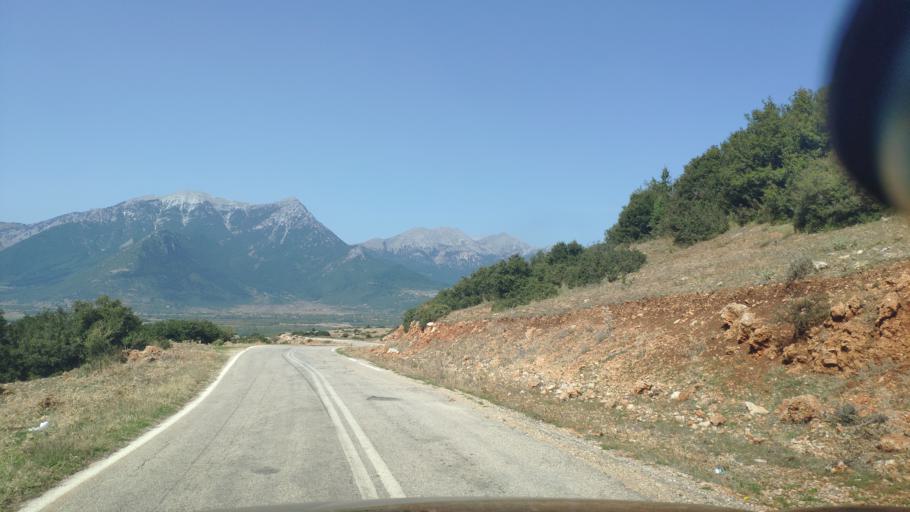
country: GR
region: West Greece
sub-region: Nomos Achaias
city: Aiyira
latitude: 37.8799
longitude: 22.3506
